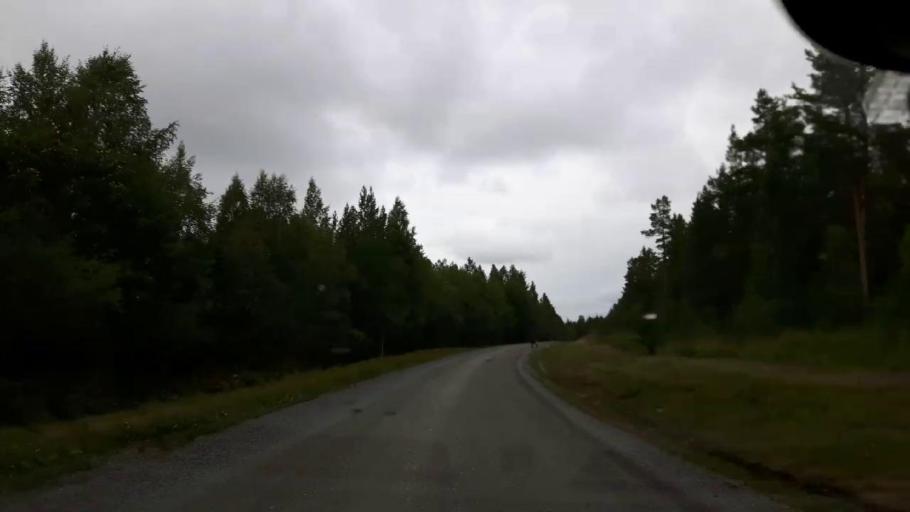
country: SE
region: Jaemtland
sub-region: OEstersunds Kommun
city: Ostersund
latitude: 63.0652
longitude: 14.5519
